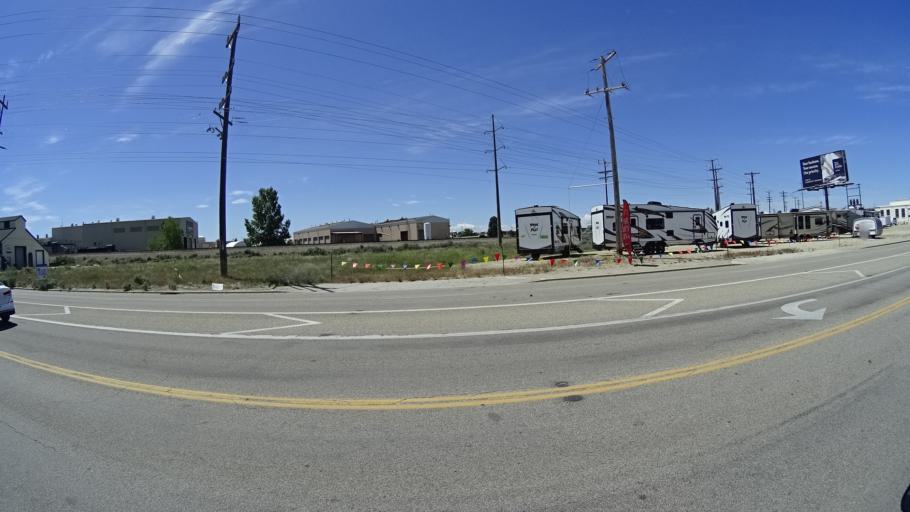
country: US
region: Idaho
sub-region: Ada County
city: Boise
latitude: 43.5609
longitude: -116.1691
